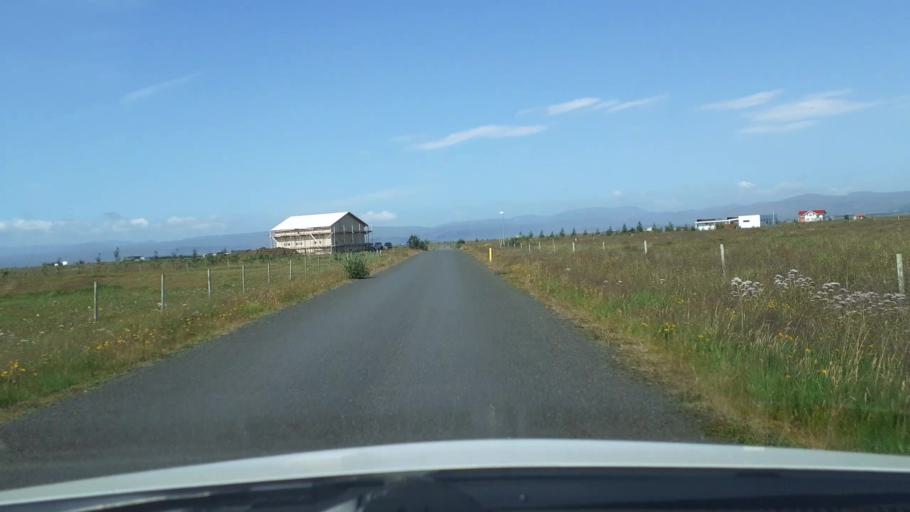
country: IS
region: South
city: Selfoss
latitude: 63.8965
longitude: -21.0814
